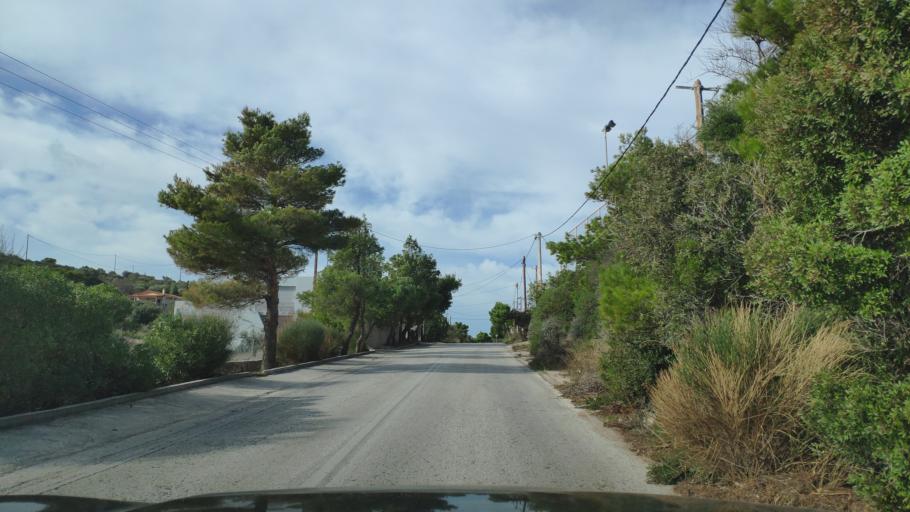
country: GR
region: Attica
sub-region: Nomarchia Anatolikis Attikis
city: Limin Mesoyaias
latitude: 37.9067
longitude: 24.0218
